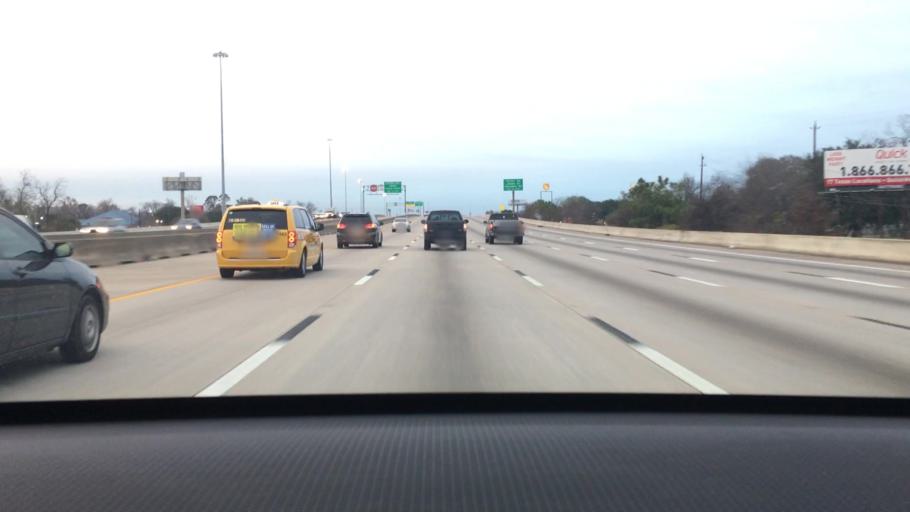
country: US
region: Texas
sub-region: Harris County
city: Houston
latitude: 29.8446
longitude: -95.3334
